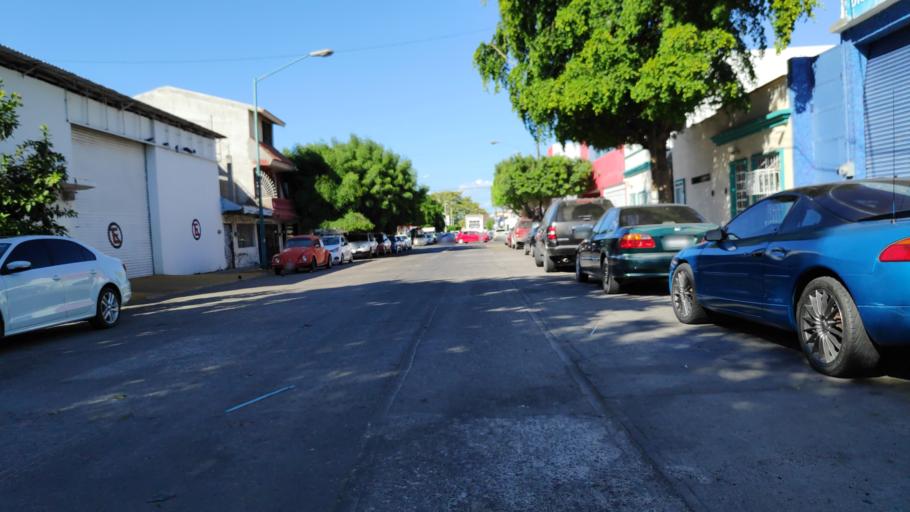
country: MX
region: Sinaloa
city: Culiacan
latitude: 24.7975
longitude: -107.3964
